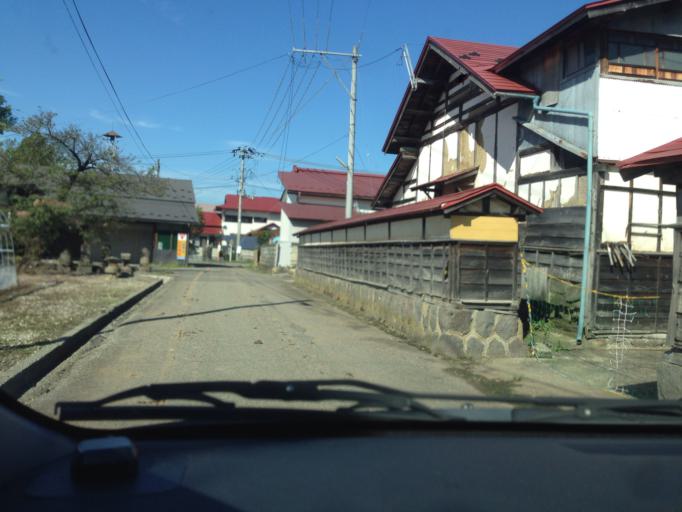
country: JP
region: Fukushima
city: Kitakata
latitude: 37.5479
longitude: 139.9168
